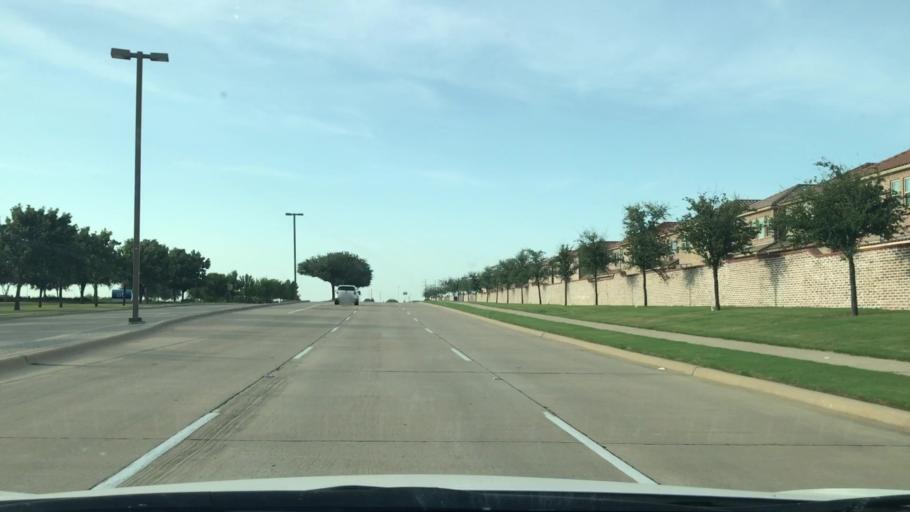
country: US
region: Texas
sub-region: Dallas County
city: Farmers Branch
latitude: 32.8985
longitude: -96.9453
